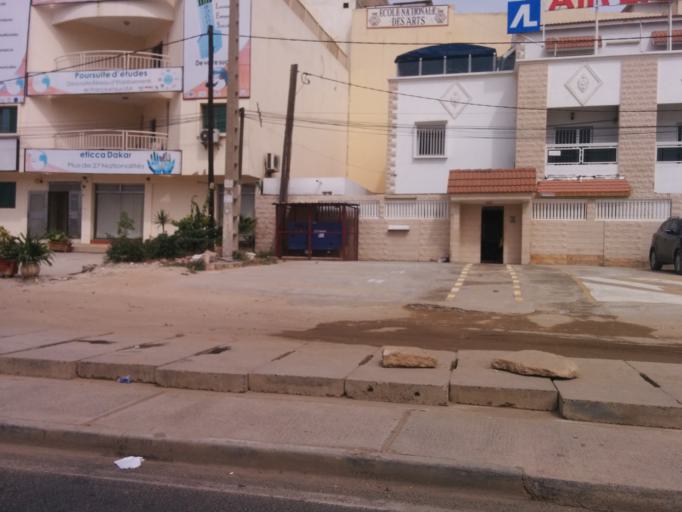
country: SN
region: Dakar
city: Mermoz Boabab
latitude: 14.7267
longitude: -17.4714
